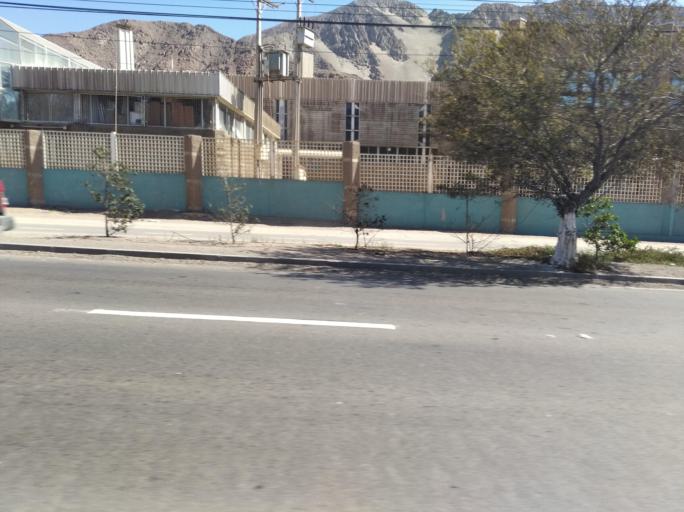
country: CL
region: Atacama
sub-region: Provincia de Copiapo
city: Copiapo
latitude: -27.3598
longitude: -70.3510
